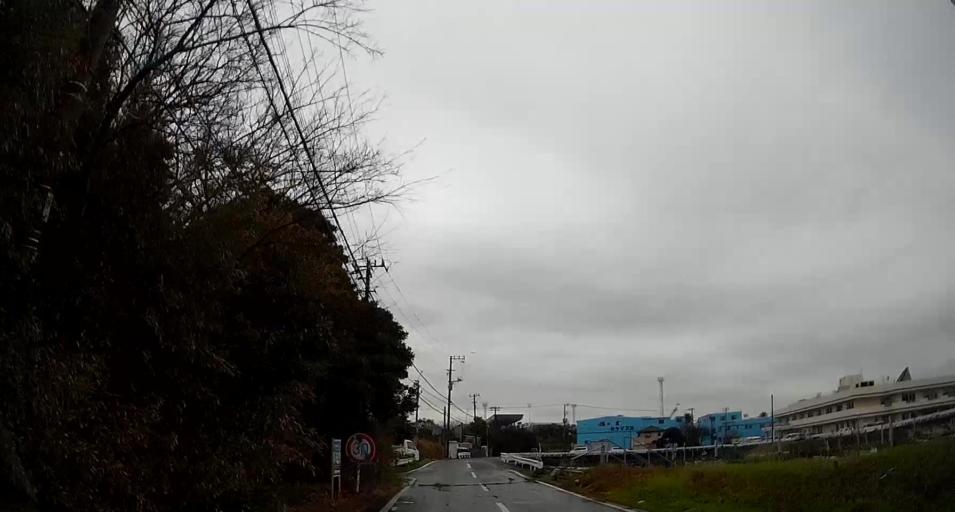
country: JP
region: Chiba
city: Kisarazu
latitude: 35.4377
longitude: 139.9211
